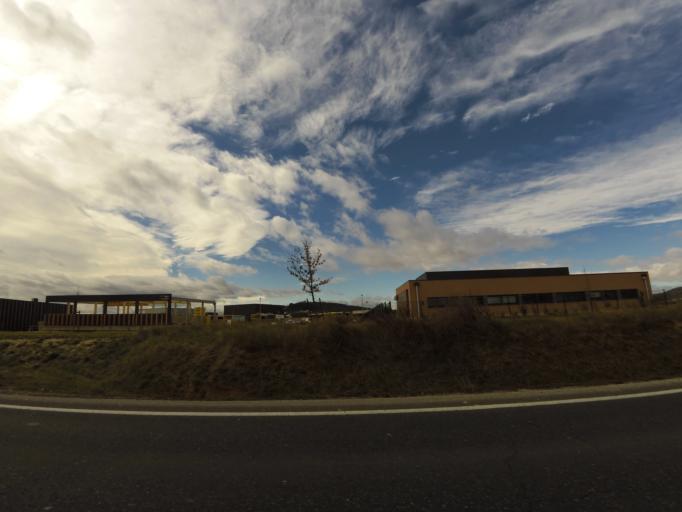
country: FR
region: Languedoc-Roussillon
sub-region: Departement du Gard
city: Calvisson
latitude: 43.7851
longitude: 4.2063
